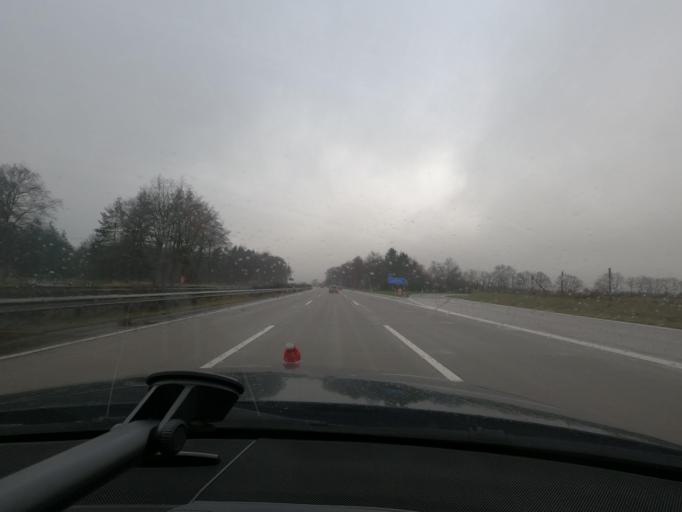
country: DE
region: Lower Saxony
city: Egestorf
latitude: 53.1899
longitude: 10.0837
